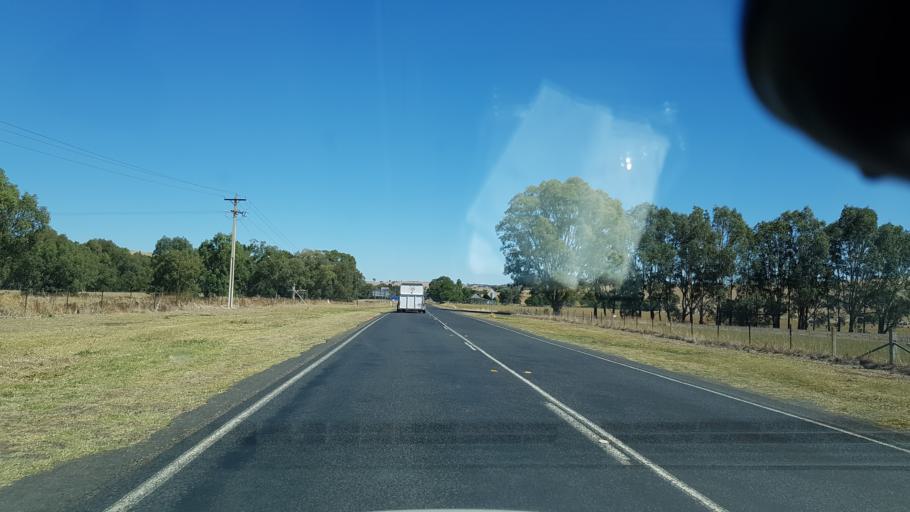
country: AU
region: New South Wales
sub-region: Gundagai
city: Gundagai
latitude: -34.8198
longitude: 148.3561
